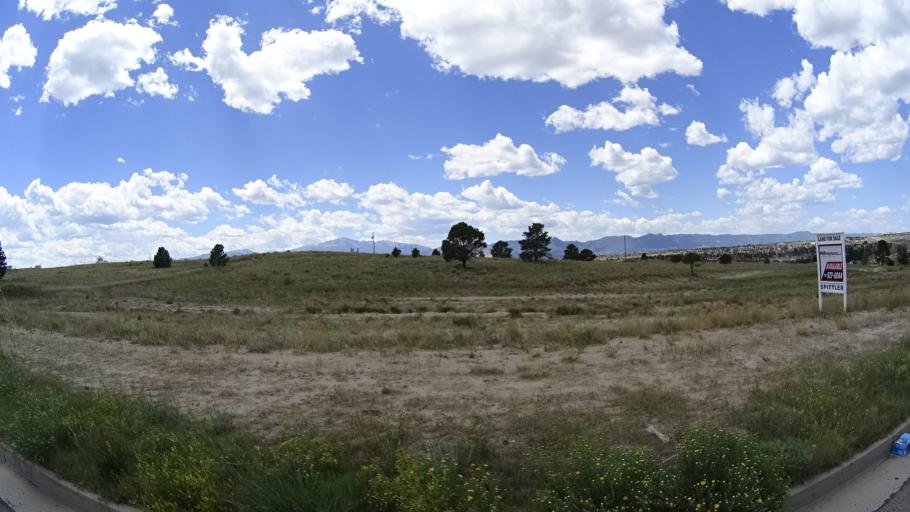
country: US
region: Colorado
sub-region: El Paso County
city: Black Forest
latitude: 38.9439
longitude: -104.7150
